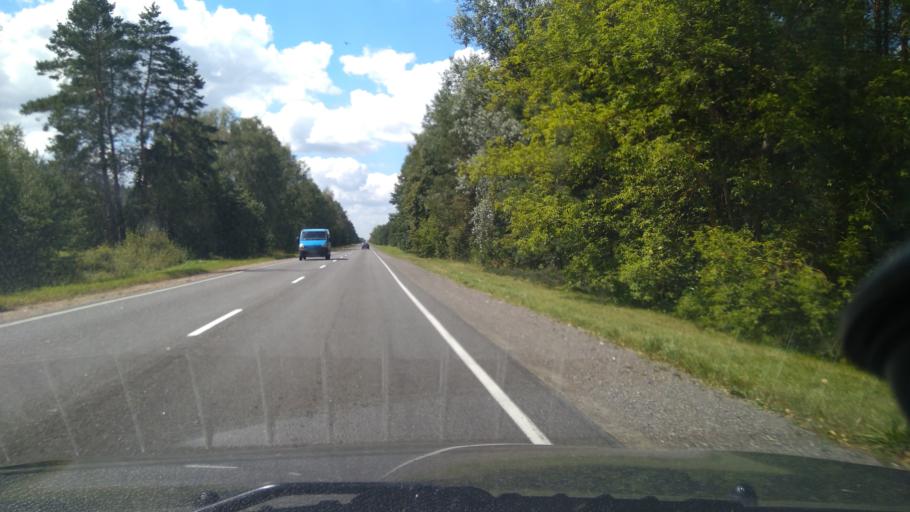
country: BY
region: Brest
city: Nyakhachava
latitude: 52.6619
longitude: 25.2417
